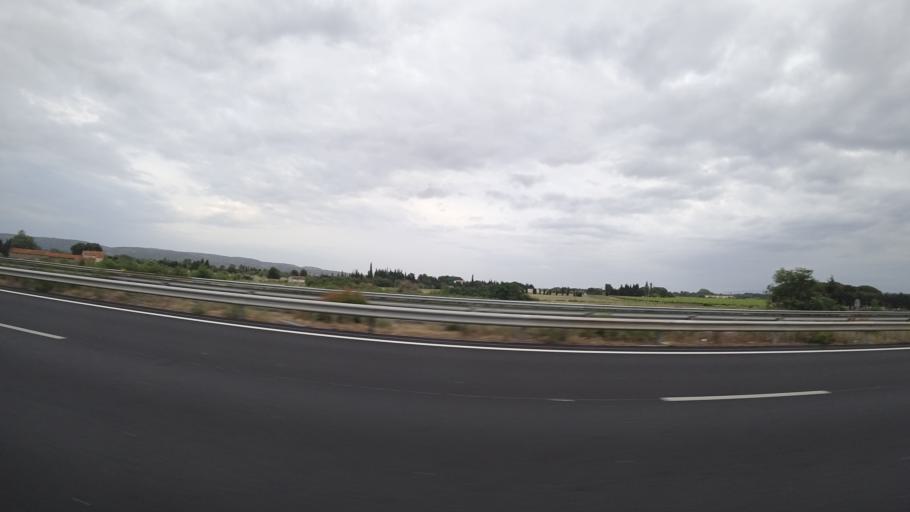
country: FR
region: Languedoc-Roussillon
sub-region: Departement de l'Aude
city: Narbonne
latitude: 43.1714
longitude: 3.0172
